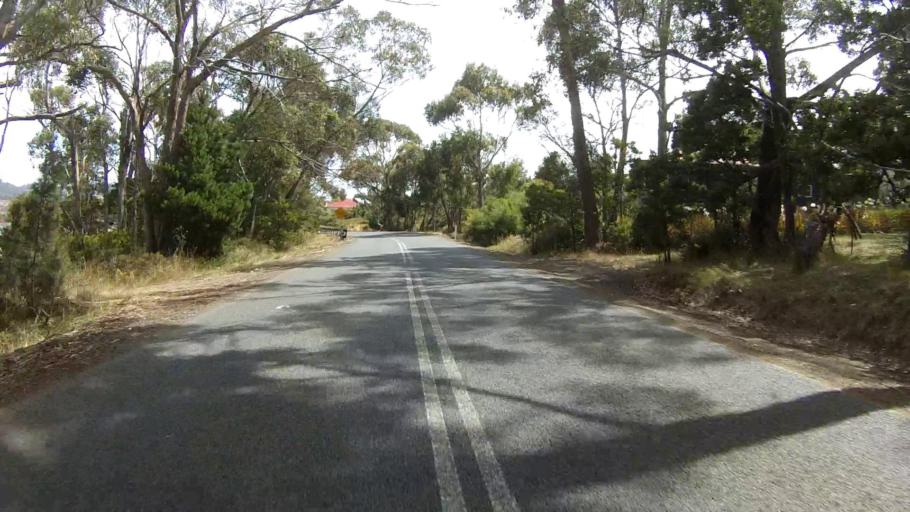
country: AU
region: Tasmania
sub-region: Huon Valley
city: Cygnet
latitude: -43.1911
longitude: 147.1018
